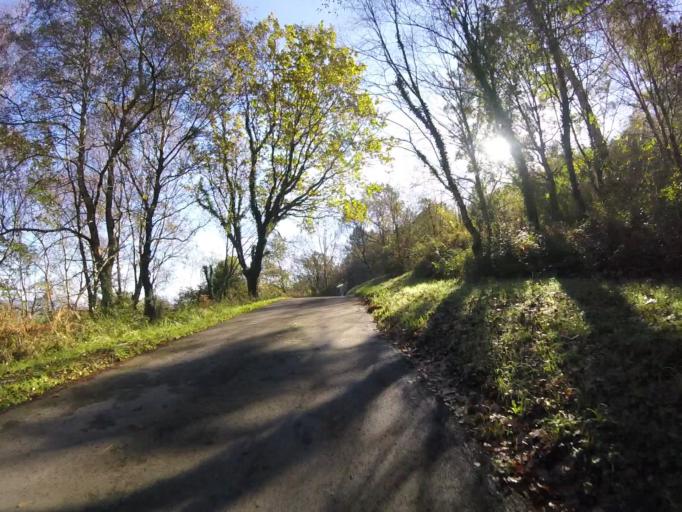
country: ES
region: Basque Country
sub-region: Provincia de Guipuzcoa
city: Usurbil
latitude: 43.2963
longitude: -2.0531
